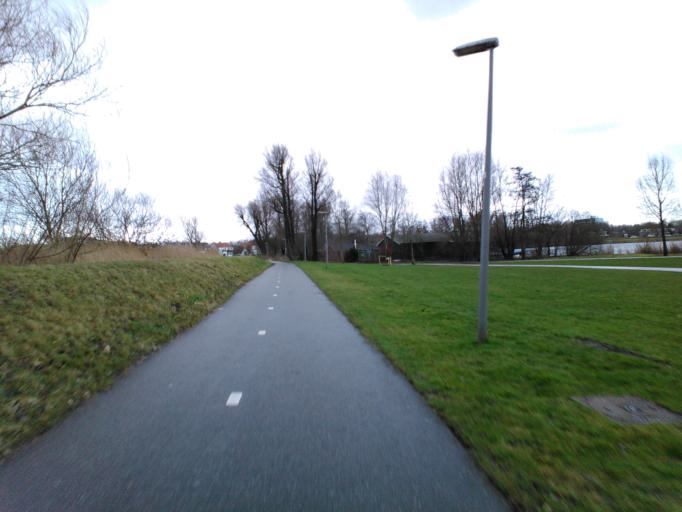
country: NL
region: South Holland
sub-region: Gemeente Rotterdam
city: Rotterdam
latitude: 51.9487
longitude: 4.4983
